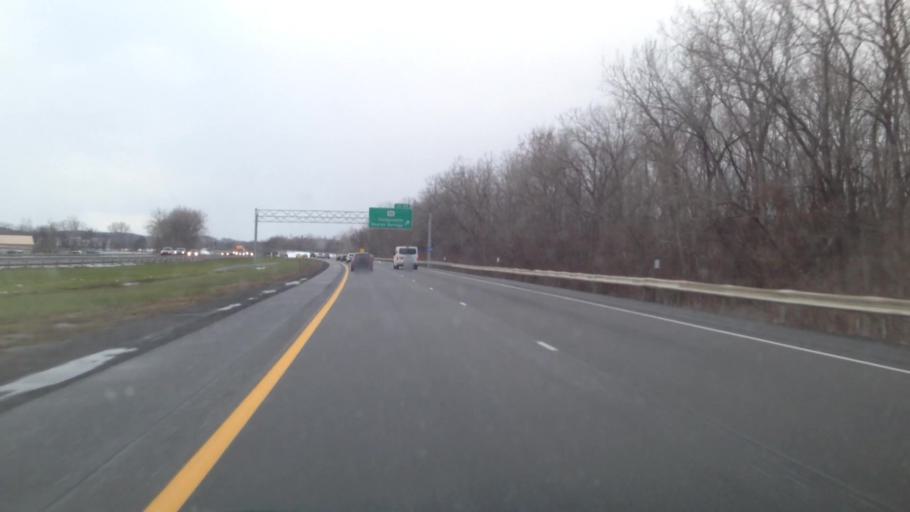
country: US
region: New York
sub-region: Montgomery County
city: Canajoharie
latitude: 42.9048
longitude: -74.5533
